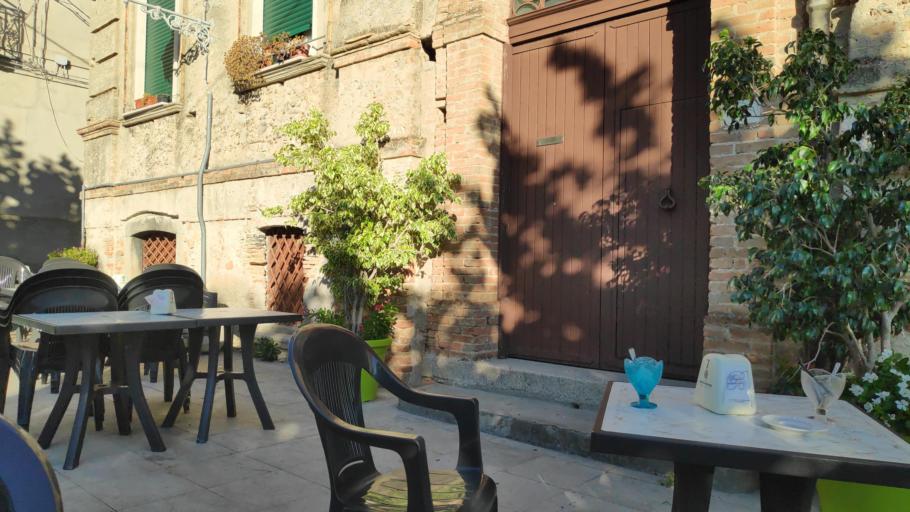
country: IT
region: Calabria
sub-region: Provincia di Reggio Calabria
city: Roccella Ionica
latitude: 38.3250
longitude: 16.4011
